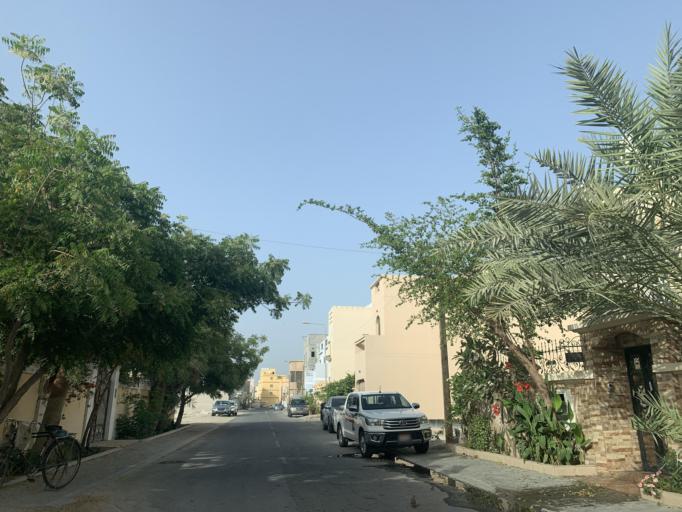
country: BH
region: Central Governorate
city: Madinat Hamad
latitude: 26.1561
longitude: 50.5085
